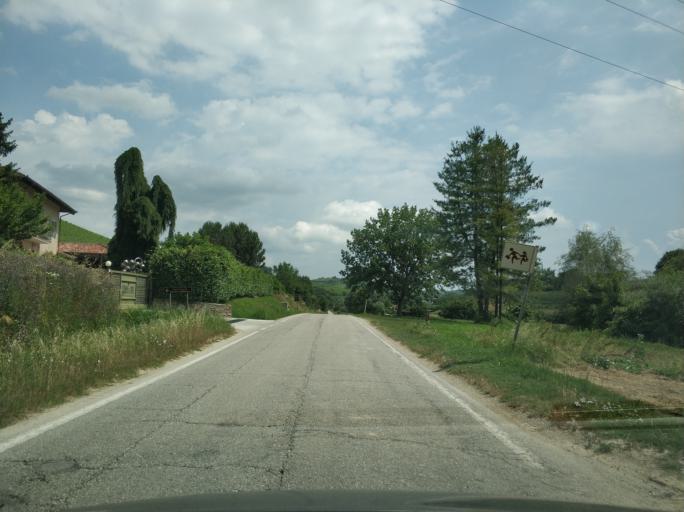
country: IT
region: Piedmont
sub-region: Provincia di Cuneo
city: Canale
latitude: 44.7885
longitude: 7.9729
